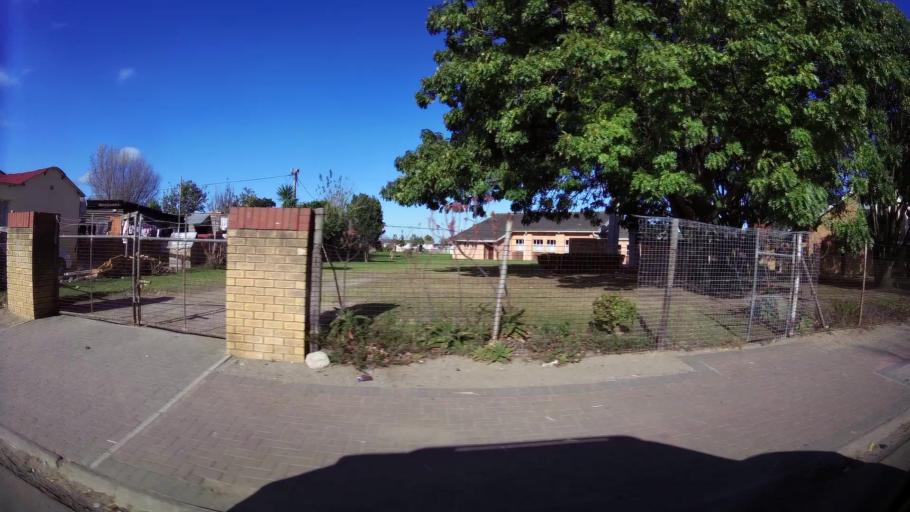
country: ZA
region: Western Cape
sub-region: Eden District Municipality
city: George
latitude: -33.9723
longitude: 22.4789
